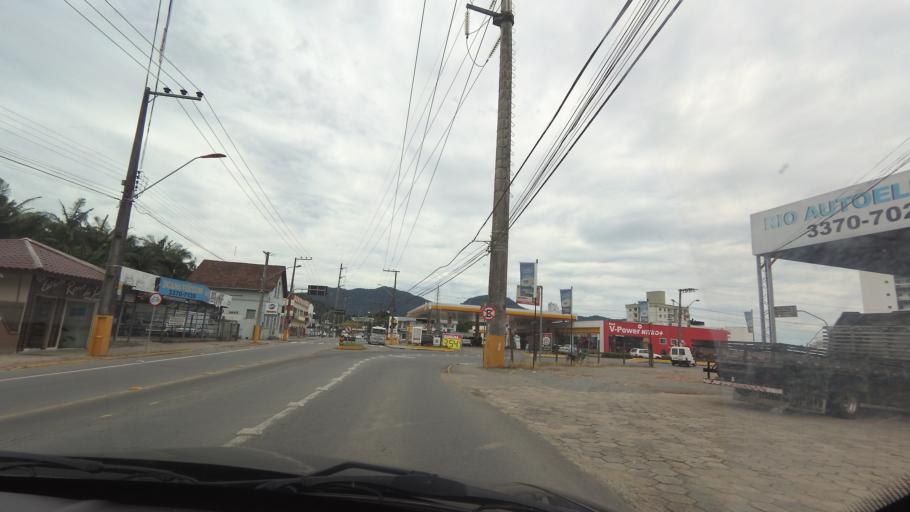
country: BR
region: Santa Catarina
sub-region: Jaragua Do Sul
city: Jaragua do Sul
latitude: -26.5004
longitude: -49.0881
